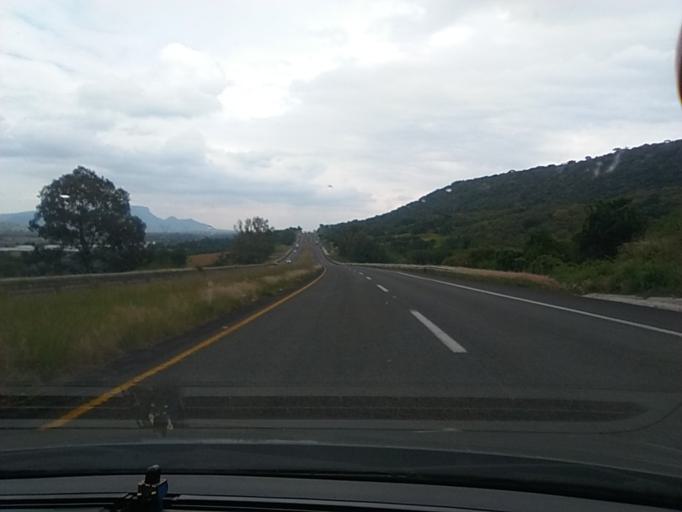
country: MX
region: Jalisco
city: Ocotlan
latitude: 20.4216
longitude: -102.7660
